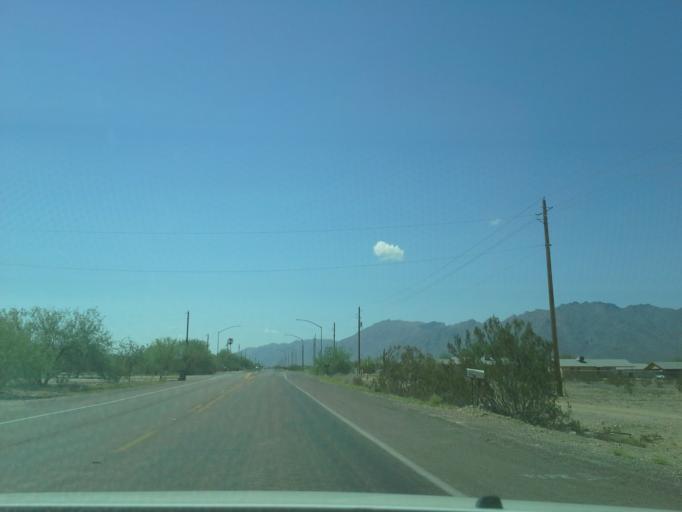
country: US
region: Arizona
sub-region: Maricopa County
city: Laveen
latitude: 33.3168
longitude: -112.1692
